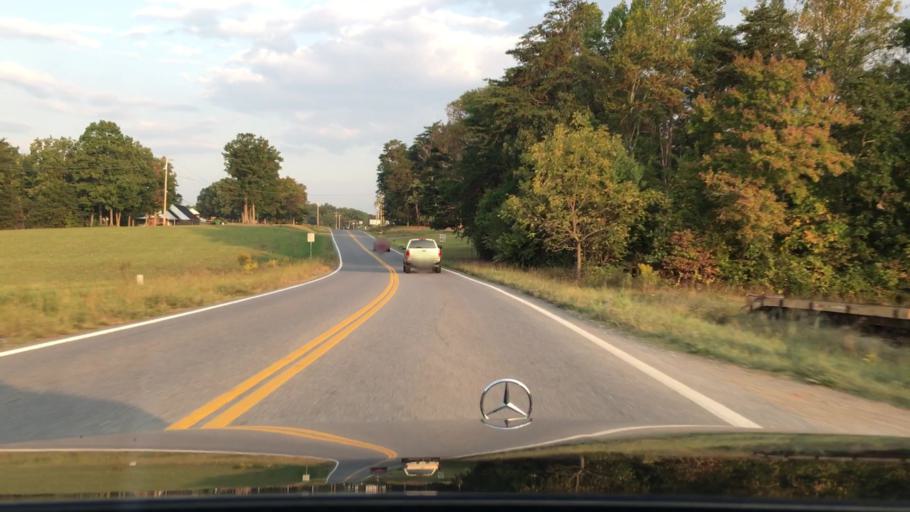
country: US
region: Virginia
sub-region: Campbell County
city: Timberlake
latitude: 37.3115
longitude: -79.2197
